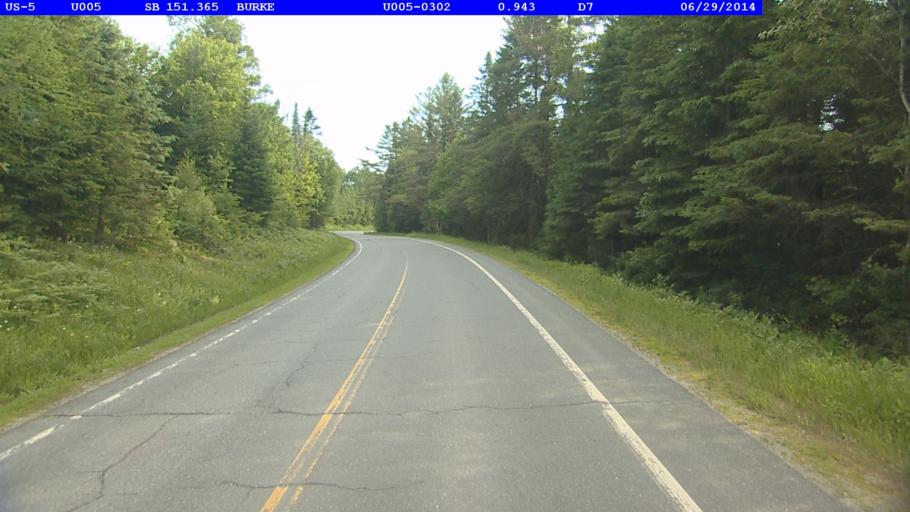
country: US
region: Vermont
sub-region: Caledonia County
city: Lyndonville
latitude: 44.5989
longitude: -71.9737
